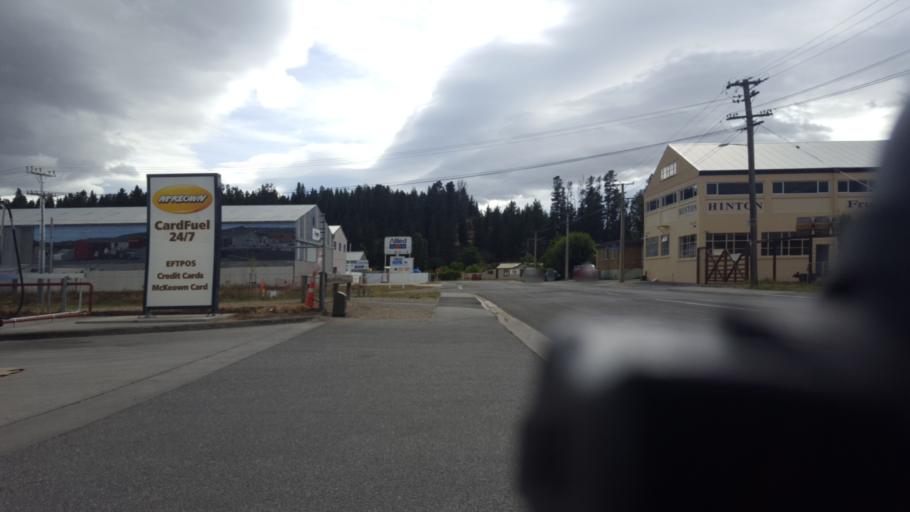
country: NZ
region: Otago
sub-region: Queenstown-Lakes District
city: Wanaka
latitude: -45.2460
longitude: 169.3949
